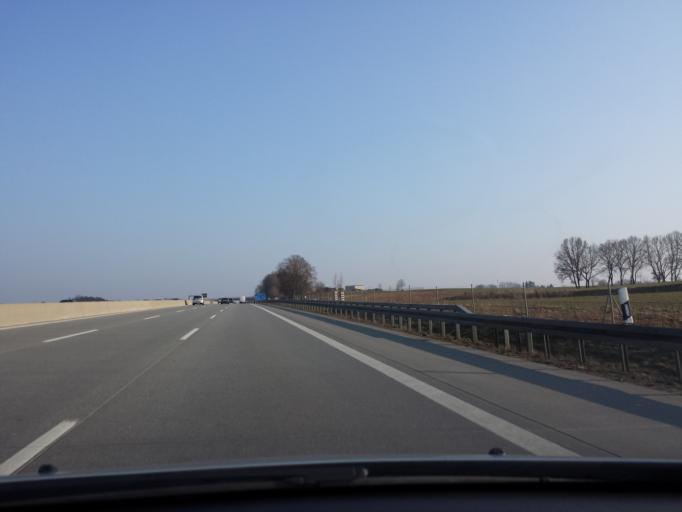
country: DE
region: Bavaria
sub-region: Swabia
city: Dasing
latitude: 48.3892
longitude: 11.0733
